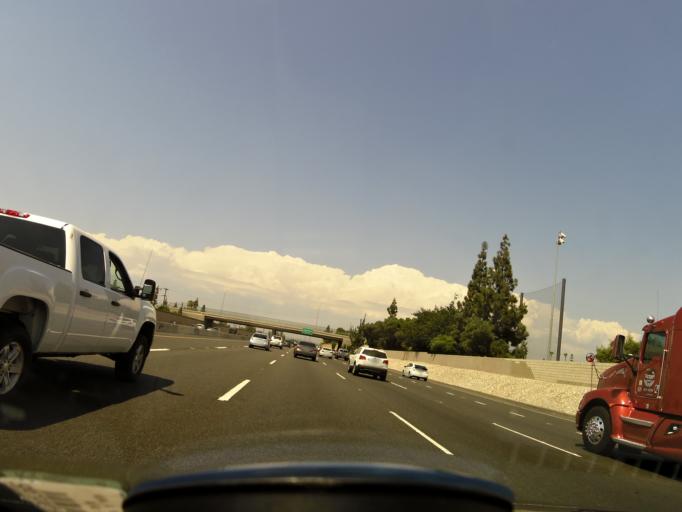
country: US
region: California
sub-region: Orange County
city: Villa Park
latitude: 33.8005
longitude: -117.8313
